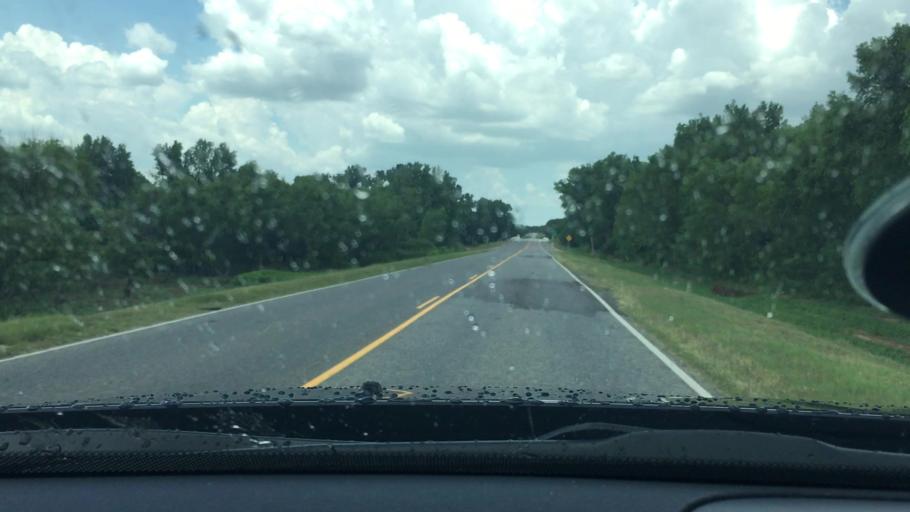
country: US
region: Oklahoma
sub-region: Johnston County
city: Tishomingo
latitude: 34.2166
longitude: -96.7032
